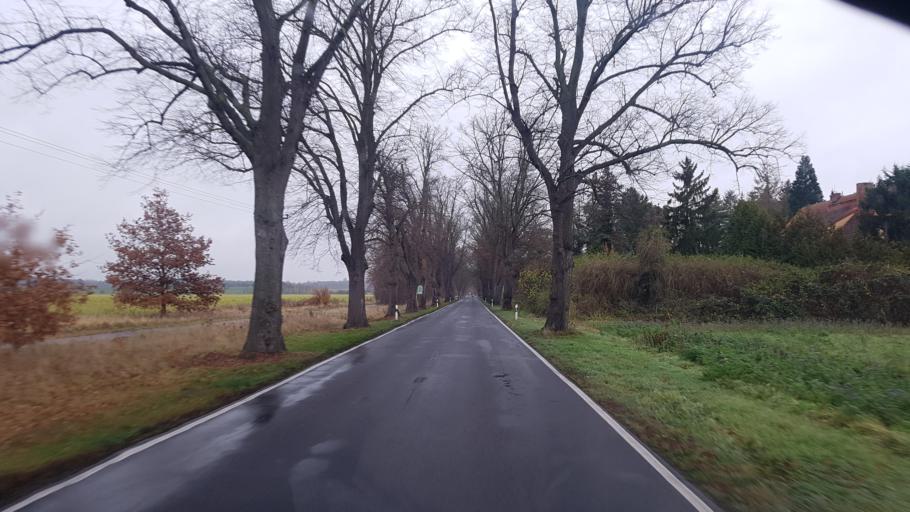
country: DE
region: Brandenburg
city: Brandenburg an der Havel
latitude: 52.4308
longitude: 12.6024
